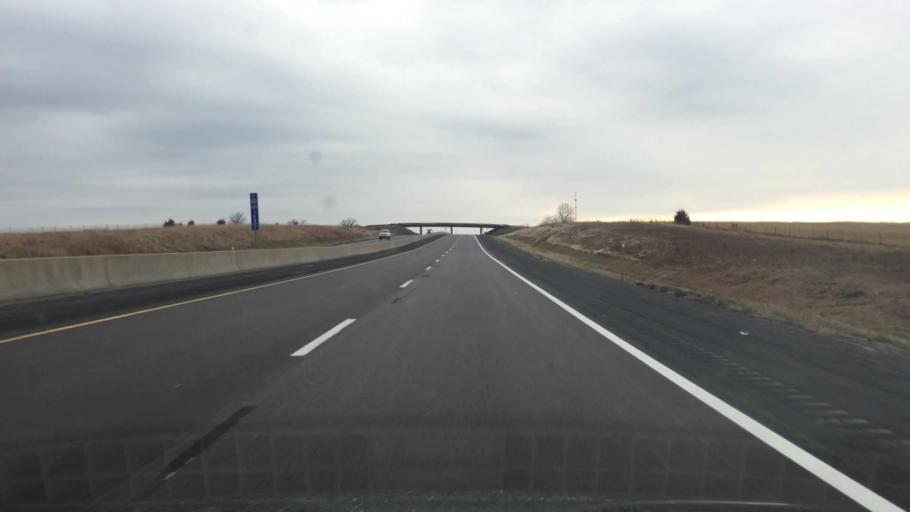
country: US
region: Kansas
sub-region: Osage County
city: Osage City
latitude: 38.7500
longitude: -95.9426
